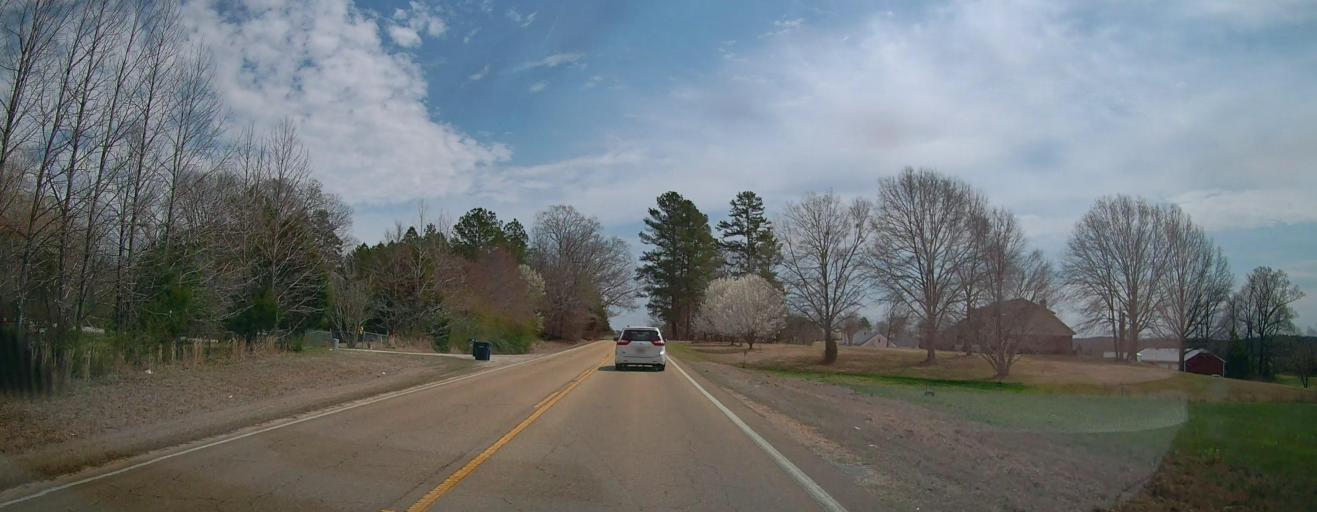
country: US
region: Mississippi
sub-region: Benton County
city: Ashland
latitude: 34.6188
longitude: -89.2141
